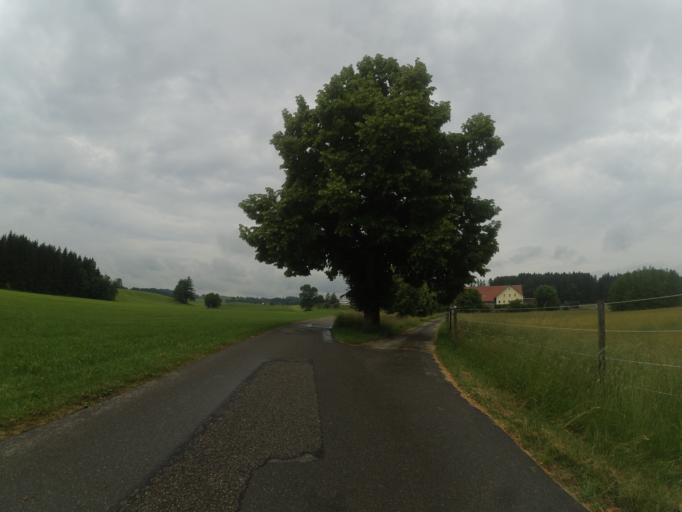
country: DE
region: Baden-Wuerttemberg
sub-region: Tuebingen Region
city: Kisslegg
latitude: 47.7649
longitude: 9.8583
